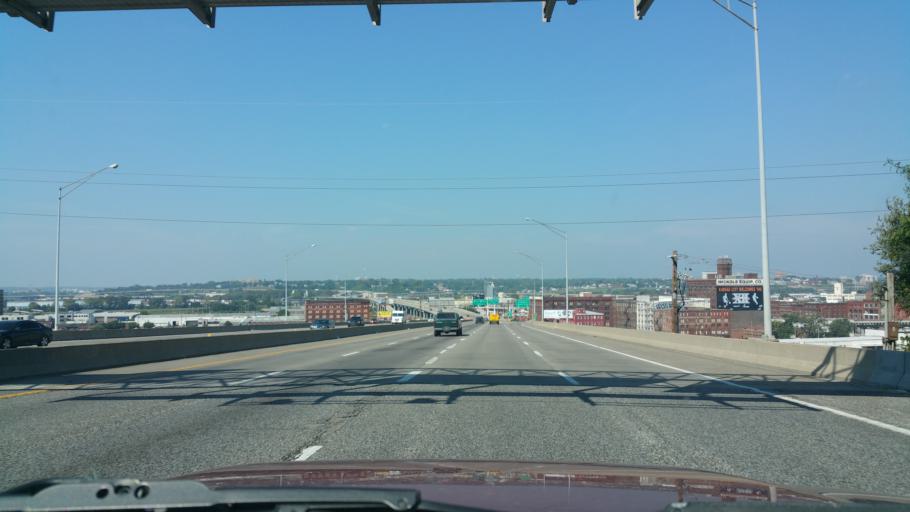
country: US
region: Missouri
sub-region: Jackson County
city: Kansas City
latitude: 39.0970
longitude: -94.5958
